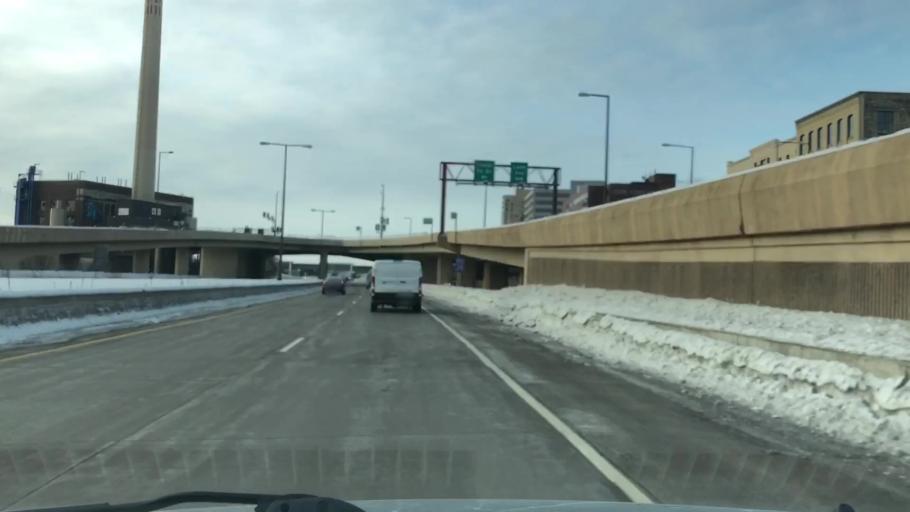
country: US
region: Minnesota
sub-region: Saint Louis County
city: Duluth
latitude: 46.7875
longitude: -92.0959
